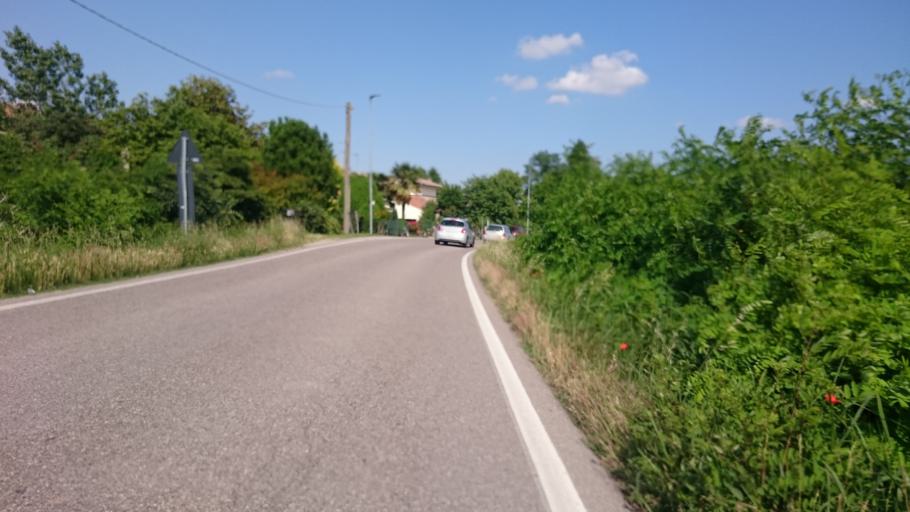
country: IT
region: Lombardy
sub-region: Provincia di Mantova
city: Mottella
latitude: 45.1558
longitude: 10.8450
